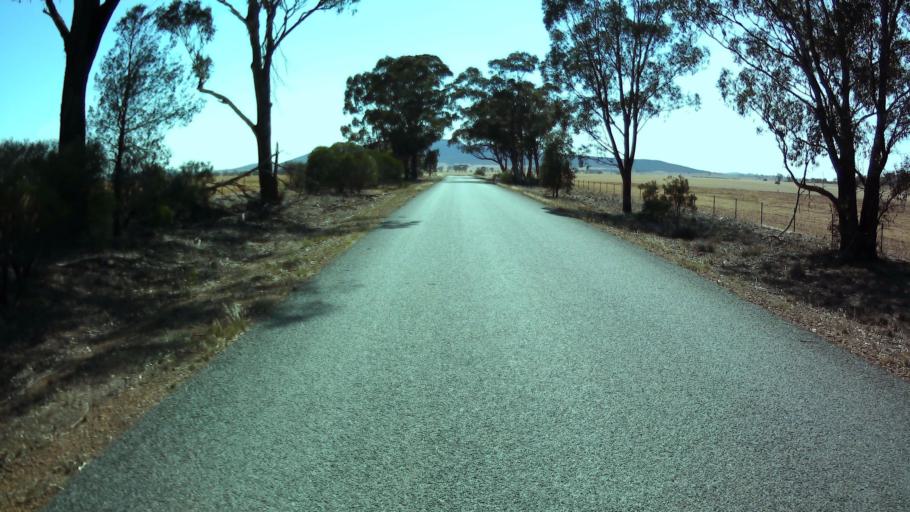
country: AU
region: New South Wales
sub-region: Weddin
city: Grenfell
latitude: -33.7534
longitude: 147.8620
